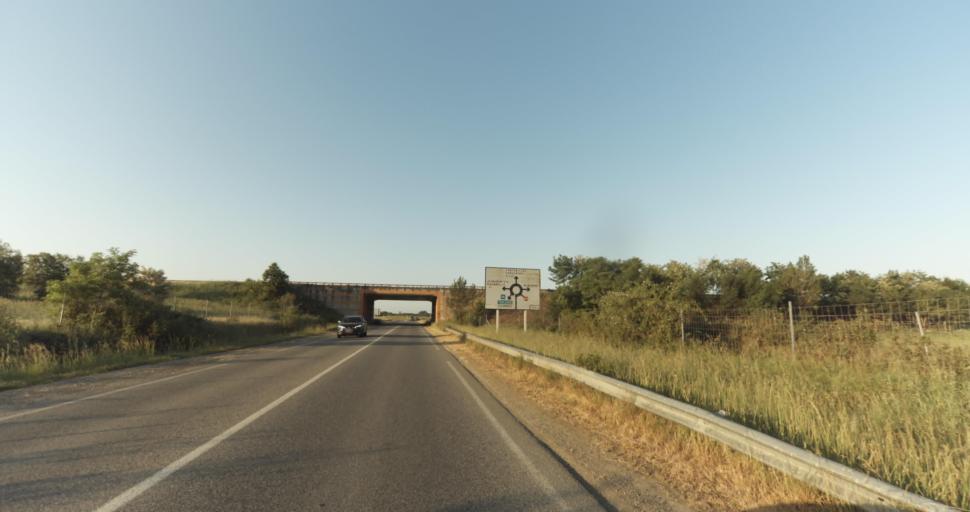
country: FR
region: Midi-Pyrenees
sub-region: Departement de la Haute-Garonne
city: Leguevin
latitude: 43.5830
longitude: 1.2183
